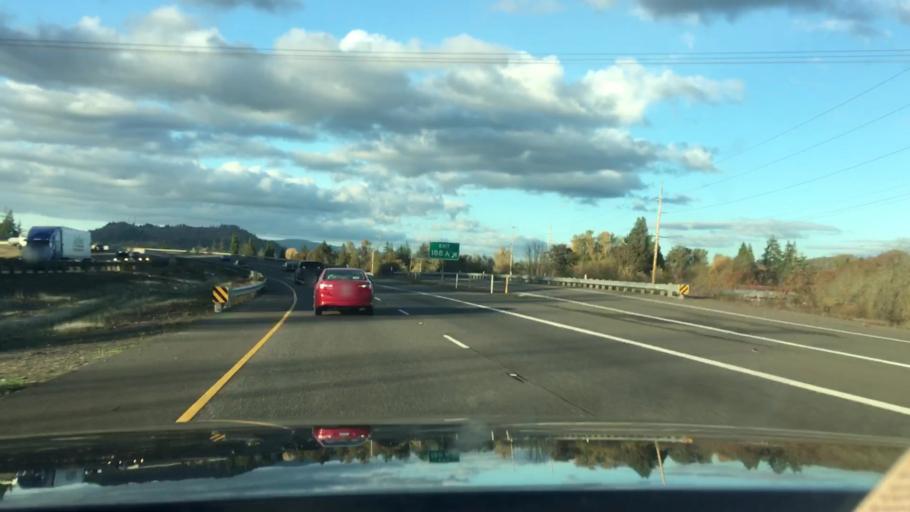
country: US
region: Oregon
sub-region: Lane County
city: Springfield
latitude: 43.9912
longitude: -123.0060
